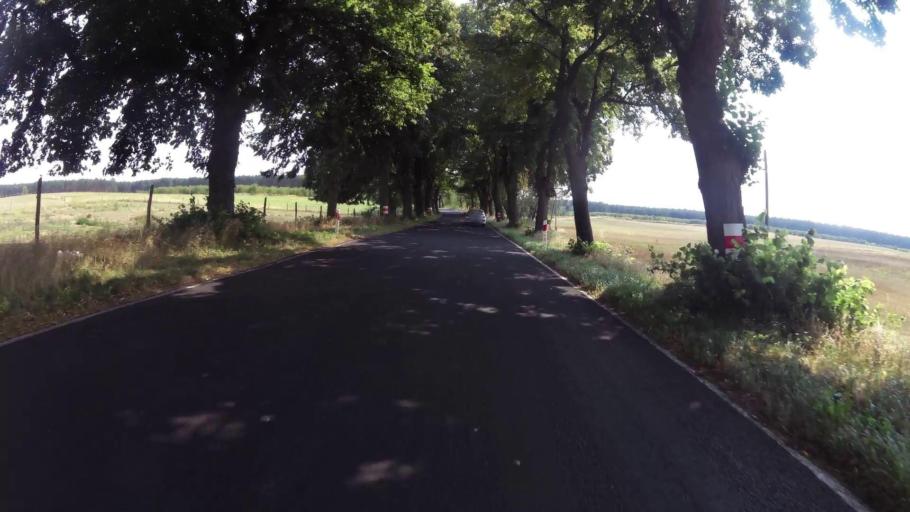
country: PL
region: West Pomeranian Voivodeship
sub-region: Powiat gryfinski
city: Moryn
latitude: 52.8400
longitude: 14.4046
